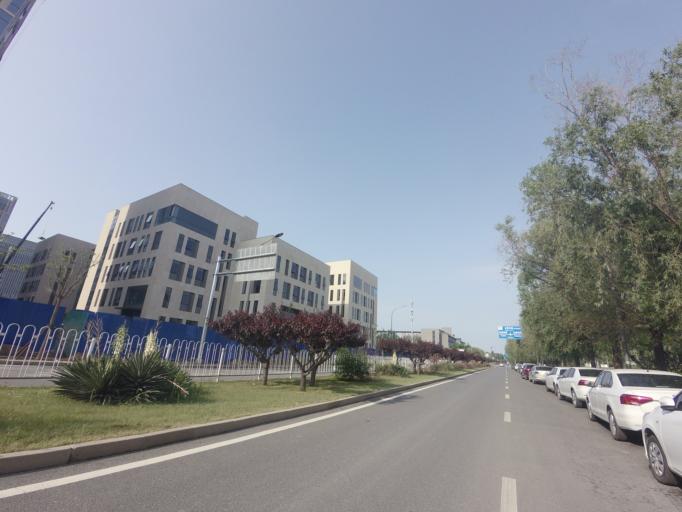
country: CN
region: Beijing
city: Xibeiwang
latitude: 40.0714
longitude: 116.2438
